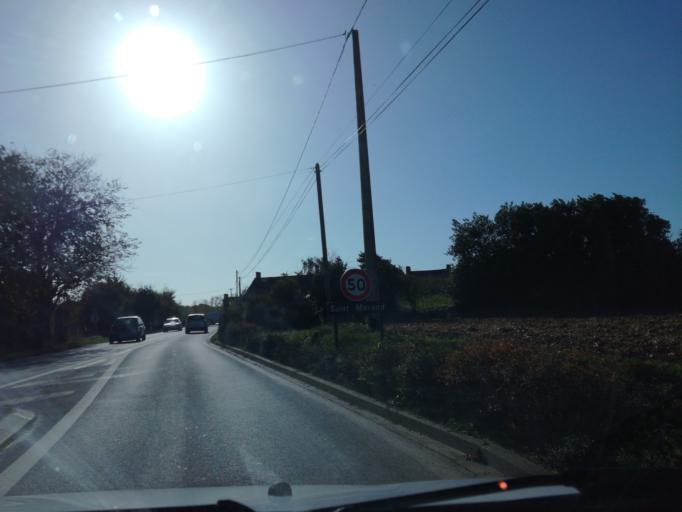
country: FR
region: Brittany
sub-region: Departement d'Ille-et-Vilaine
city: Martigne-Ferchaud
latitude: 47.8023
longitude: -1.2811
